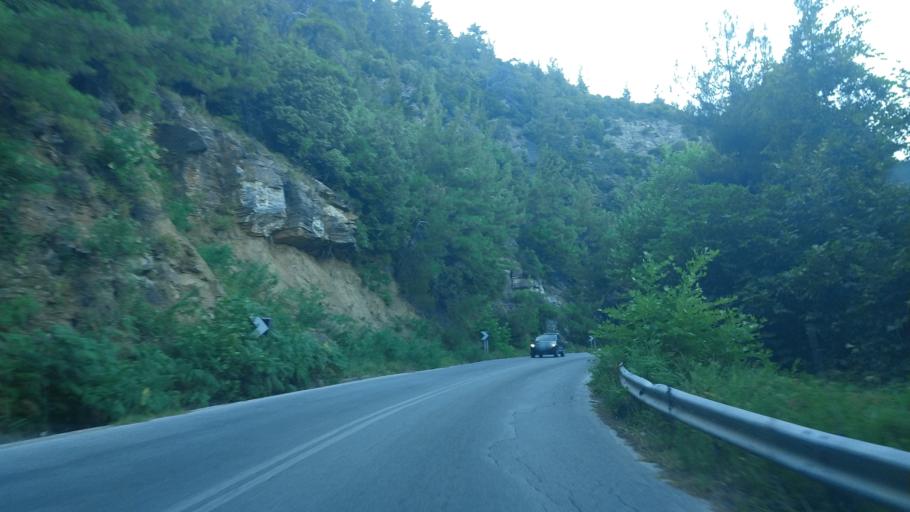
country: GR
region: East Macedonia and Thrace
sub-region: Nomos Kavalas
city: Potamia
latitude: 40.7246
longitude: 24.7326
